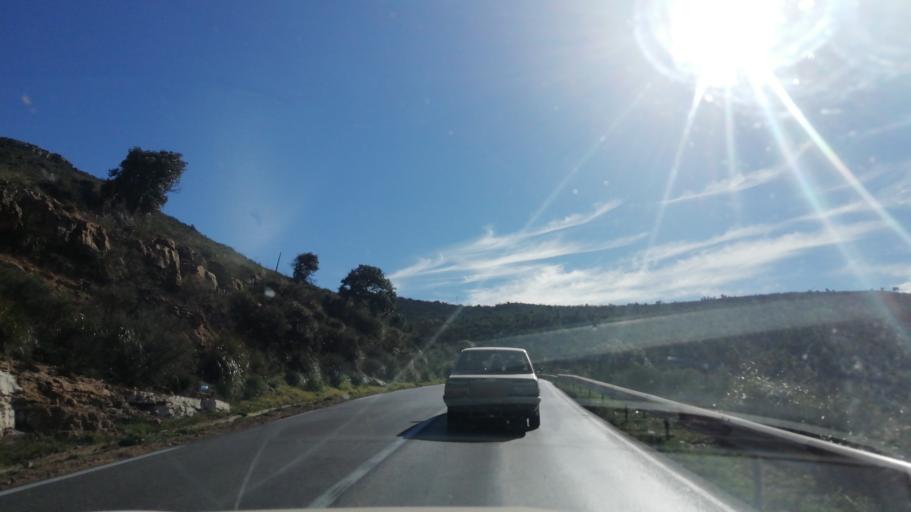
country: DZ
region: Tlemcen
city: Mansoura
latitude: 34.8462
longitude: -1.3633
